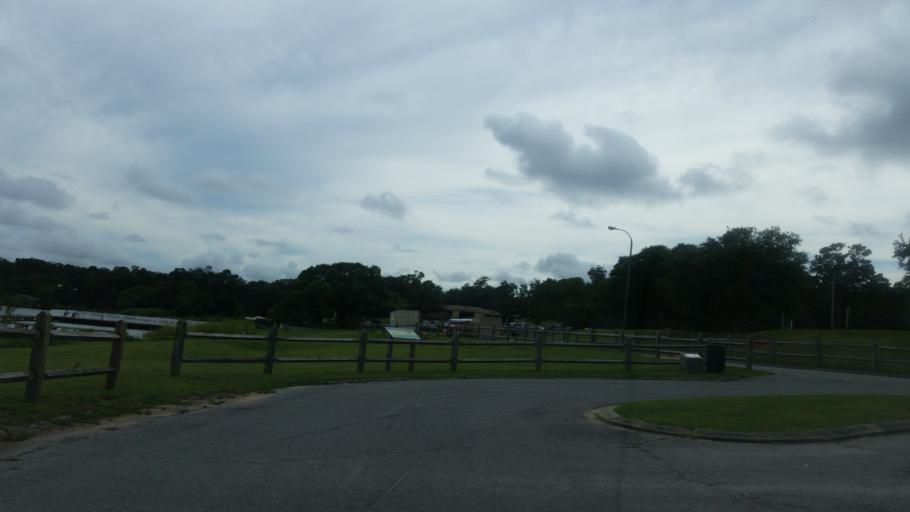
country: US
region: Florida
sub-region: Escambia County
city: East Pensacola Heights
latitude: 30.4321
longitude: -87.1890
